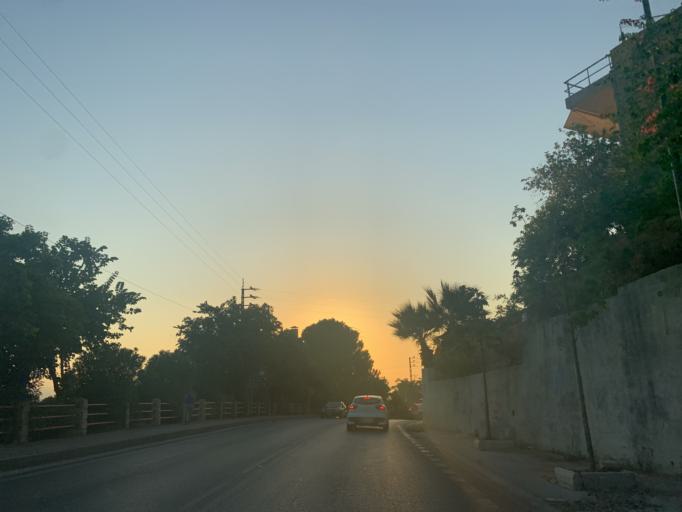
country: LB
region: Mont-Liban
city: Djounie
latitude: 33.9616
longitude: 35.6241
